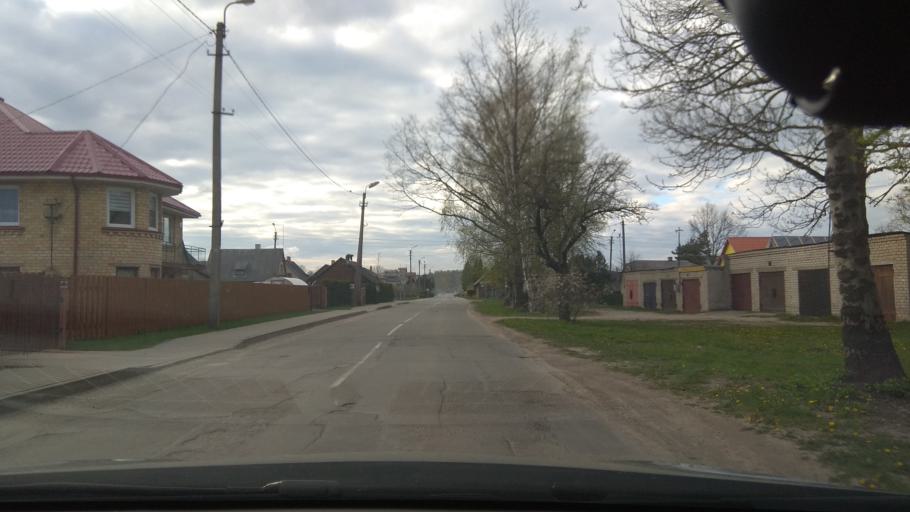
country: LT
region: Siauliu apskritis
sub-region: Joniskis
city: Joniskis
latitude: 56.2453
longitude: 23.6137
